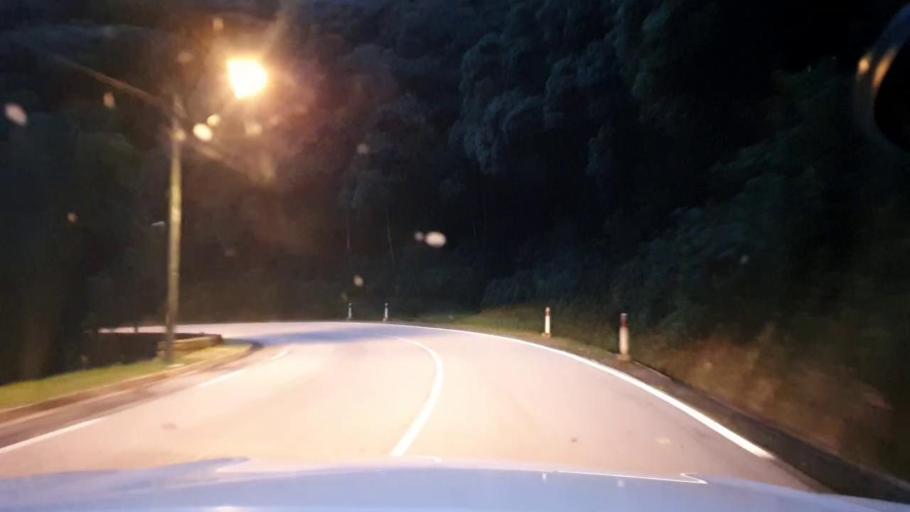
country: RW
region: Southern Province
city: Nzega
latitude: -2.5316
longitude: 29.3873
